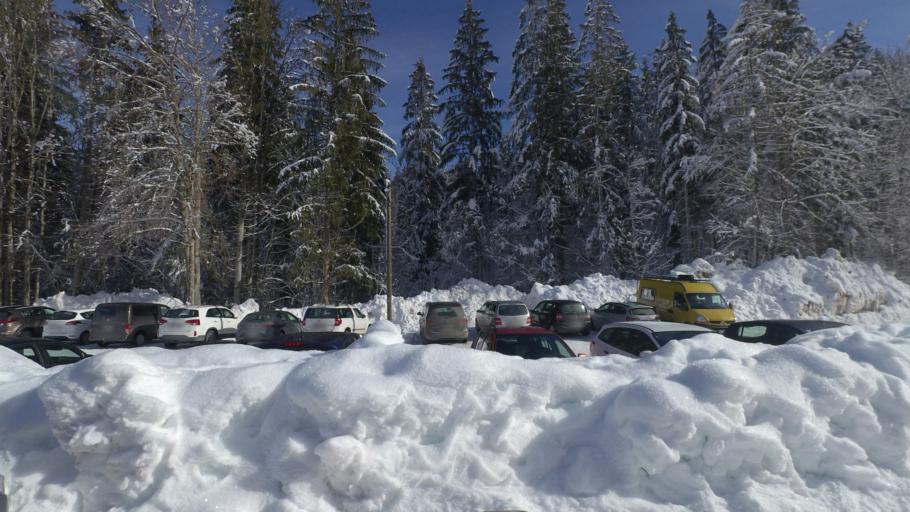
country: DE
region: Bavaria
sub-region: Upper Bavaria
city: Reit im Winkl
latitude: 47.6609
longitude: 12.4790
